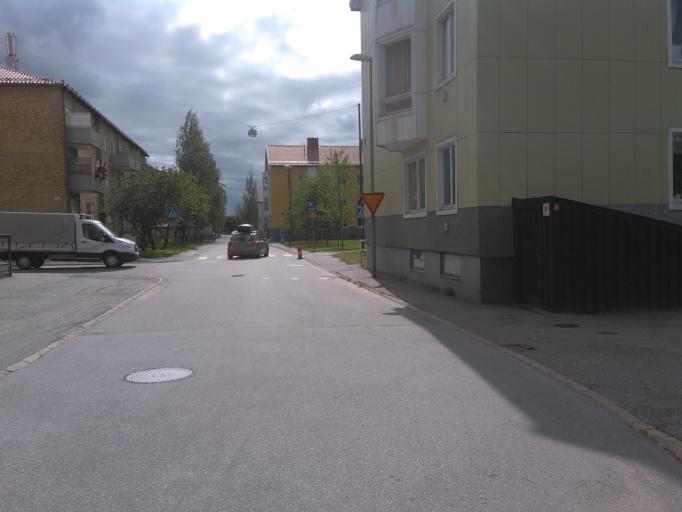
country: SE
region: Vaesterbotten
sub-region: Umea Kommun
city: Umea
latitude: 63.8294
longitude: 20.2458
